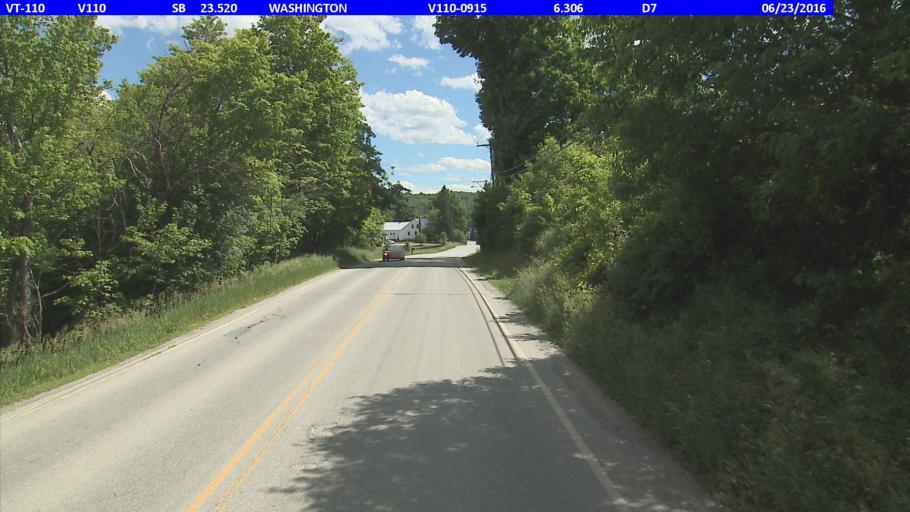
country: US
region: Vermont
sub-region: Washington County
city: South Barre
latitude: 44.1143
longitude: -72.4337
